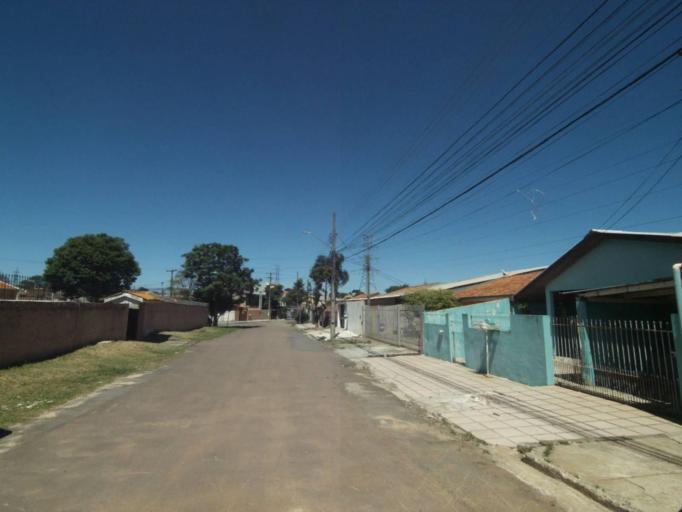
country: BR
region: Parana
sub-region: Curitiba
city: Curitiba
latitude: -25.4767
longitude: -49.3396
